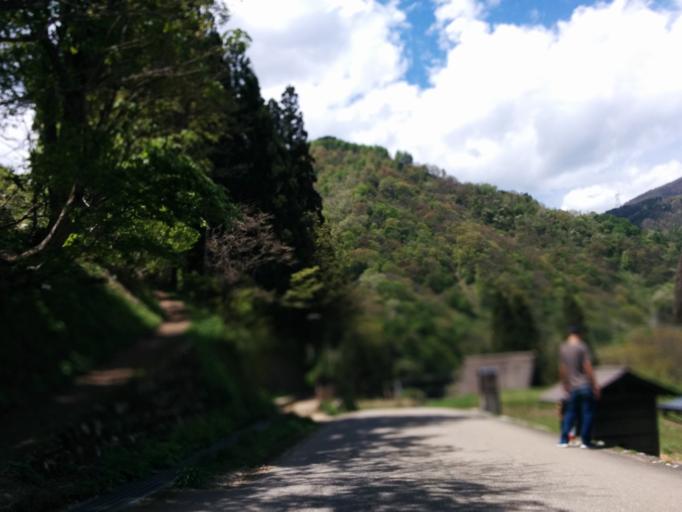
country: JP
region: Toyama
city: Fukumitsu
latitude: 36.4038
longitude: 136.8860
